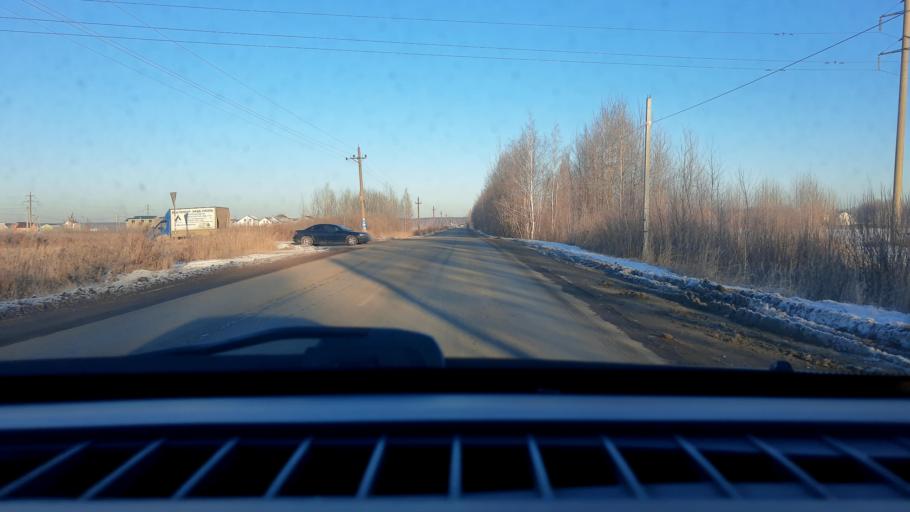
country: RU
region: Nizjnij Novgorod
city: Bor
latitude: 56.3895
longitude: 44.0787
